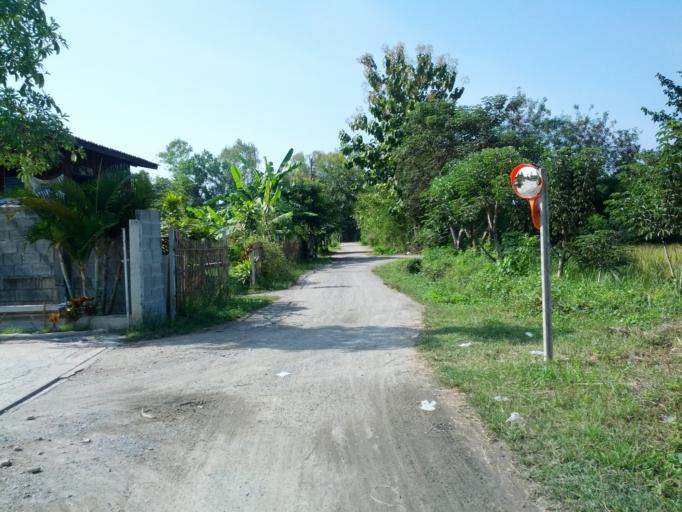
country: TH
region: Chiang Mai
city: San Kamphaeng
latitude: 18.7683
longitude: 99.1174
